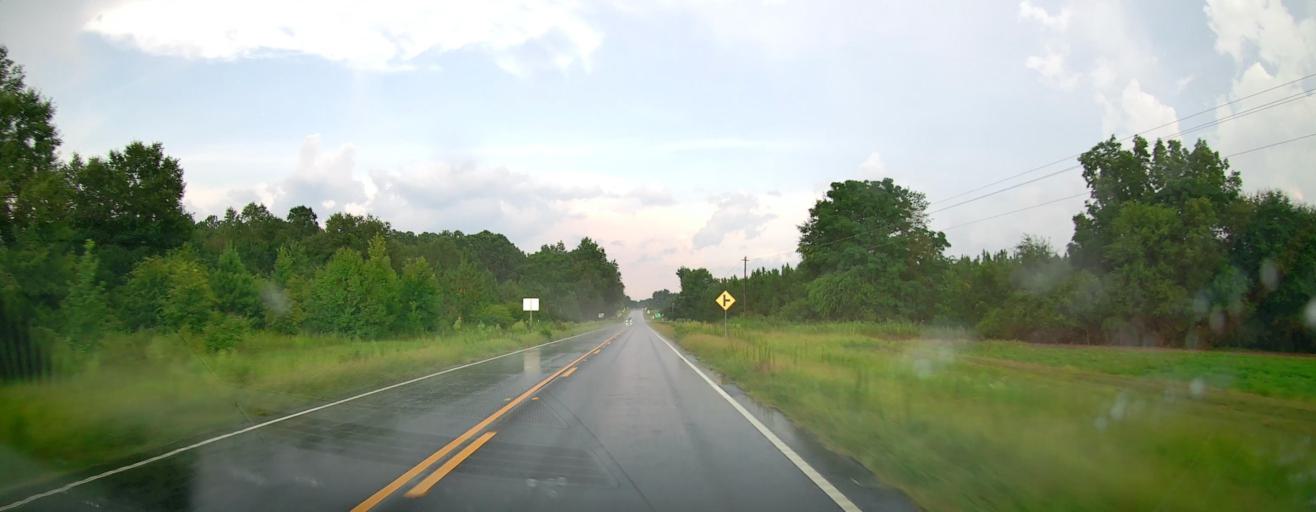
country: US
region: Georgia
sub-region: Dodge County
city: Chester
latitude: 32.5635
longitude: -83.1658
